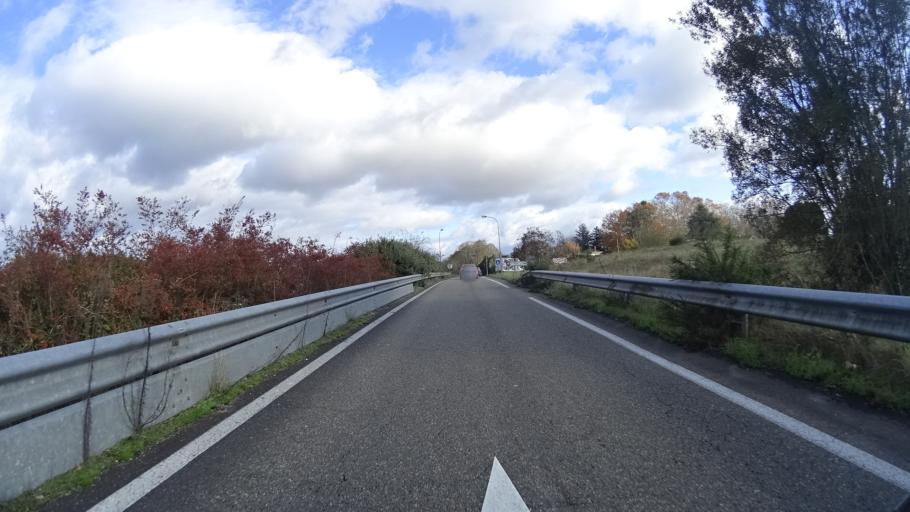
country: FR
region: Aquitaine
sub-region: Departement des Landes
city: Saint-Paul-les-Dax
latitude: 43.7444
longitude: -1.0562
